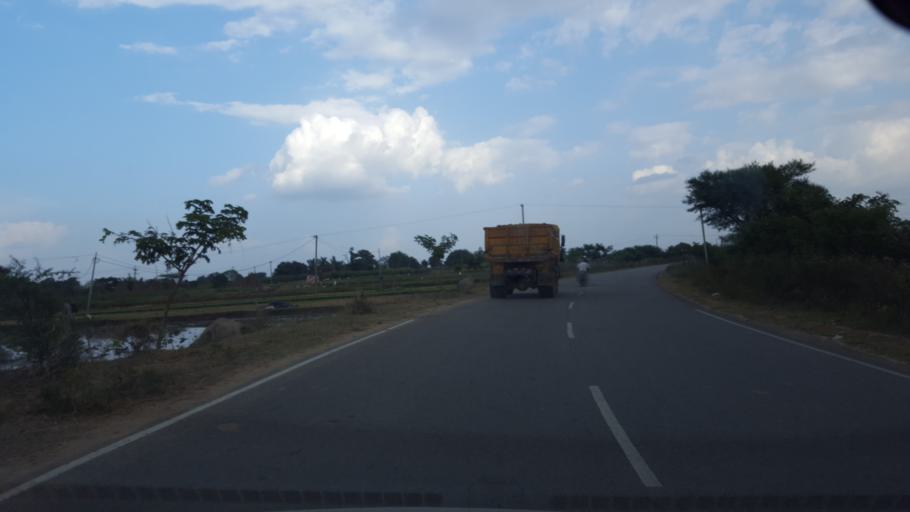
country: IN
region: Telangana
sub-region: Mahbubnagar
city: Mahbubnagar
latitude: 16.7613
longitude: 77.9525
